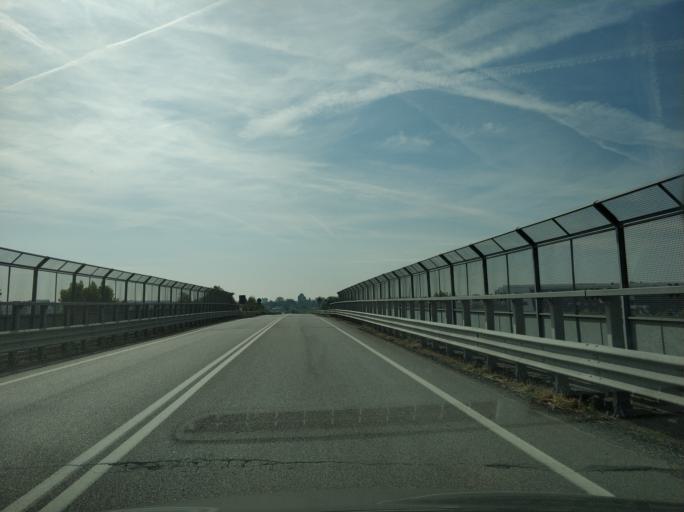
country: IT
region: Veneto
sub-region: Provincia di Padova
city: Sant'Elena
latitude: 45.2103
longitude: 11.7212
